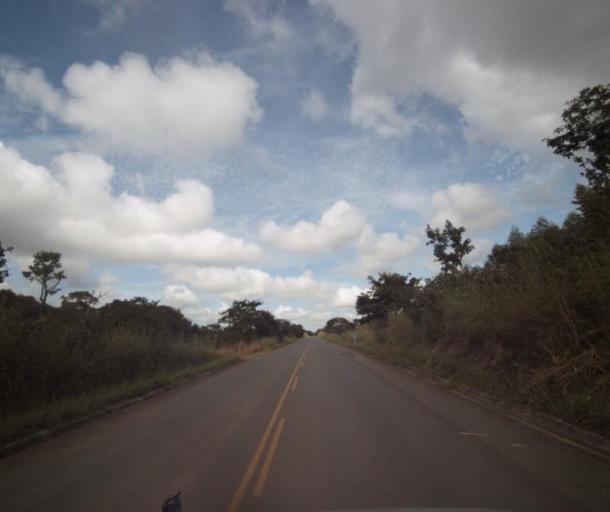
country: BR
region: Goias
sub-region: Pirenopolis
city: Pirenopolis
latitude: -15.8575
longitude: -48.7677
